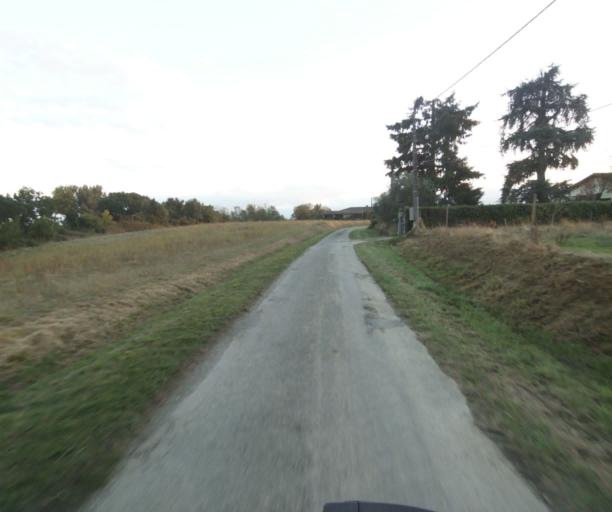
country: FR
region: Midi-Pyrenees
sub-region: Departement du Tarn-et-Garonne
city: Verdun-sur-Garonne
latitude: 43.8380
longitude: 1.2456
